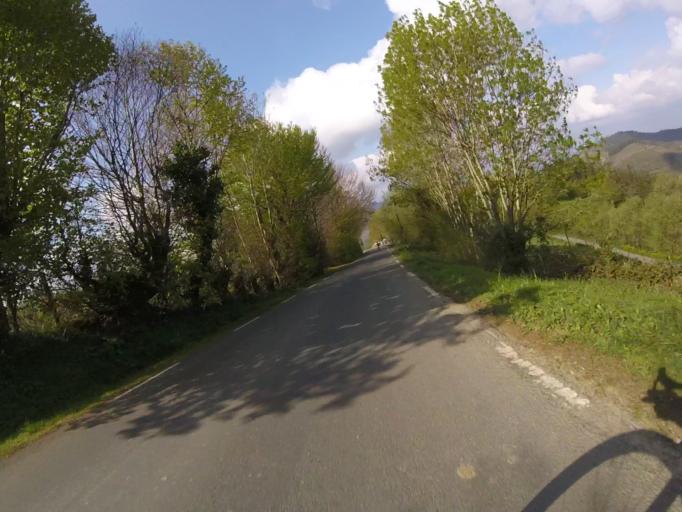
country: ES
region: Basque Country
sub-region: Provincia de Guipuzcoa
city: Azkoitia
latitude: 43.2074
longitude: -2.3350
